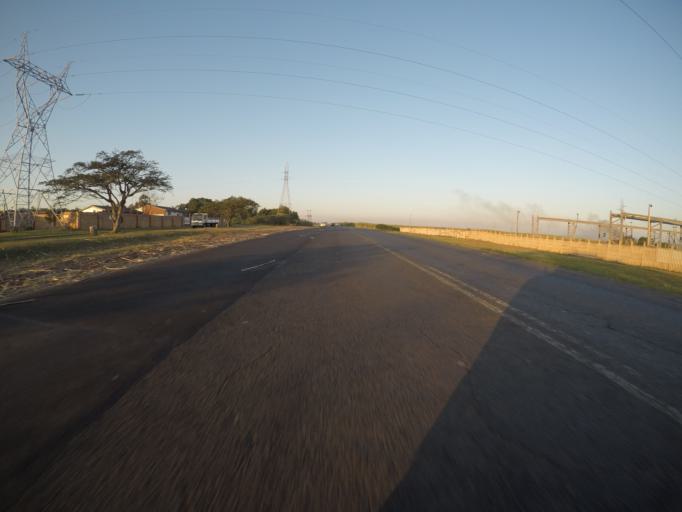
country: ZA
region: KwaZulu-Natal
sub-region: uThungulu District Municipality
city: Empangeni
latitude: -28.7811
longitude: 31.8984
